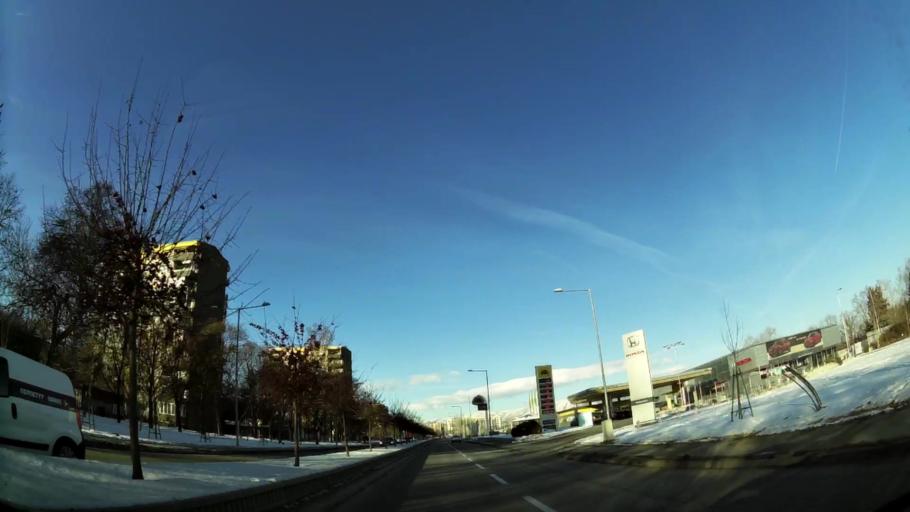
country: MK
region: Karpos
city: Skopje
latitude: 42.0073
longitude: 21.4014
